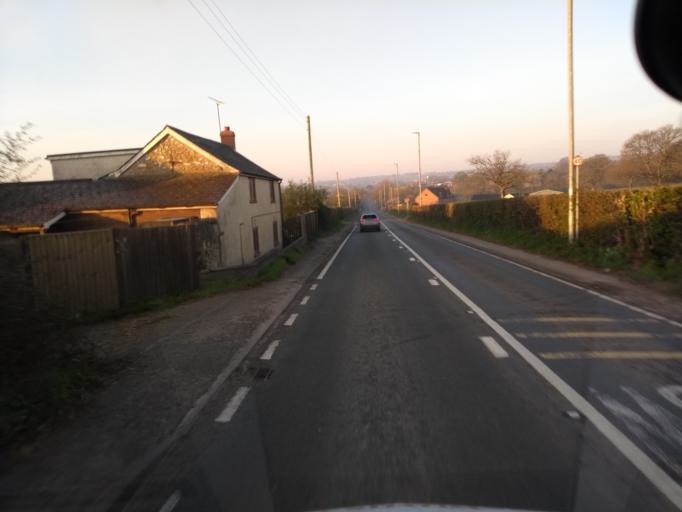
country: GB
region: England
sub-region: Somerset
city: Chard
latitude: 50.8884
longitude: -2.9495
